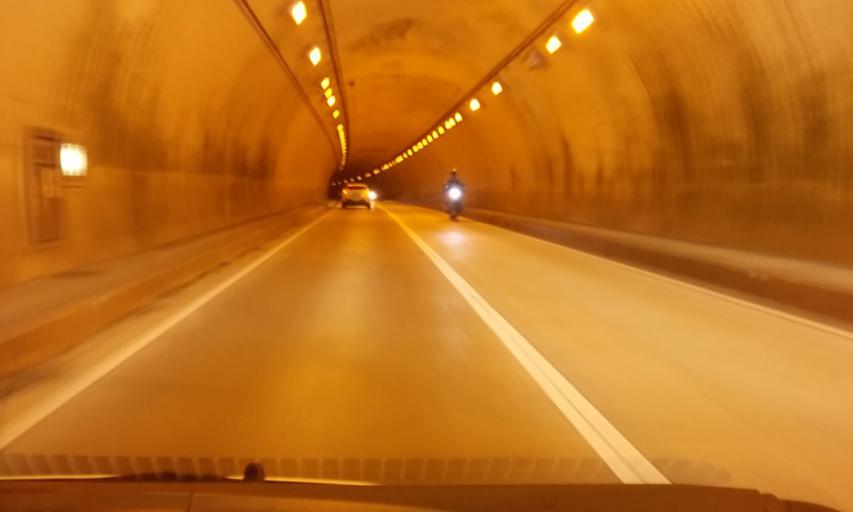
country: JP
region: Kyoto
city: Kameoka
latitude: 35.2213
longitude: 135.5717
